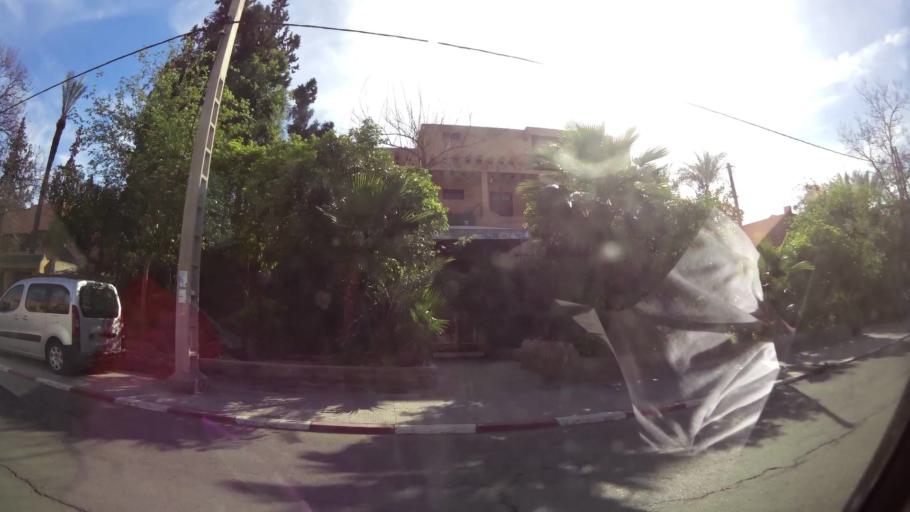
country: MA
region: Marrakech-Tensift-Al Haouz
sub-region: Marrakech
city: Marrakesh
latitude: 31.6547
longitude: -8.0098
